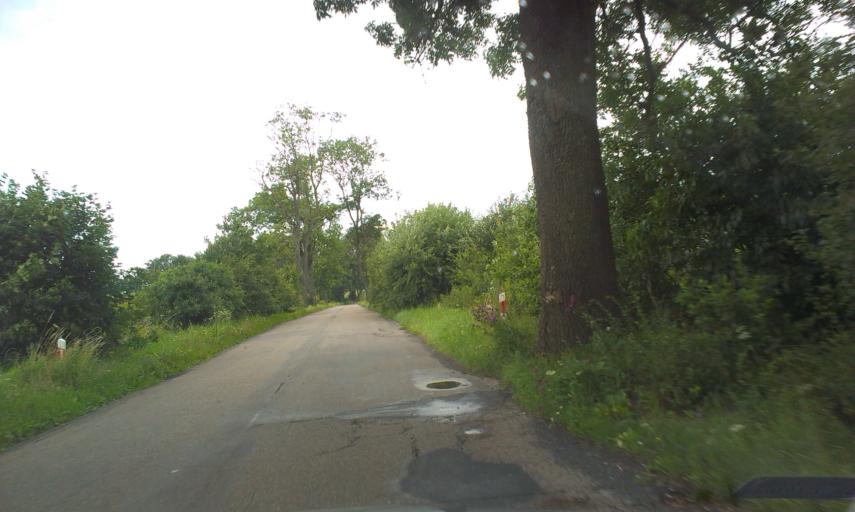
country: PL
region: West Pomeranian Voivodeship
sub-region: Powiat szczecinecki
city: Barwice
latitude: 53.7184
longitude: 16.3553
